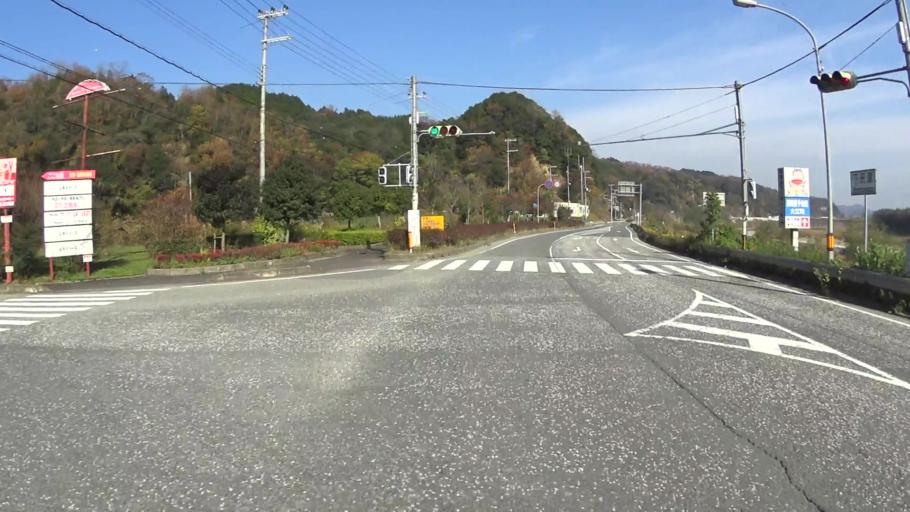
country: JP
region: Kyoto
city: Fukuchiyama
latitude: 35.3632
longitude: 135.1146
